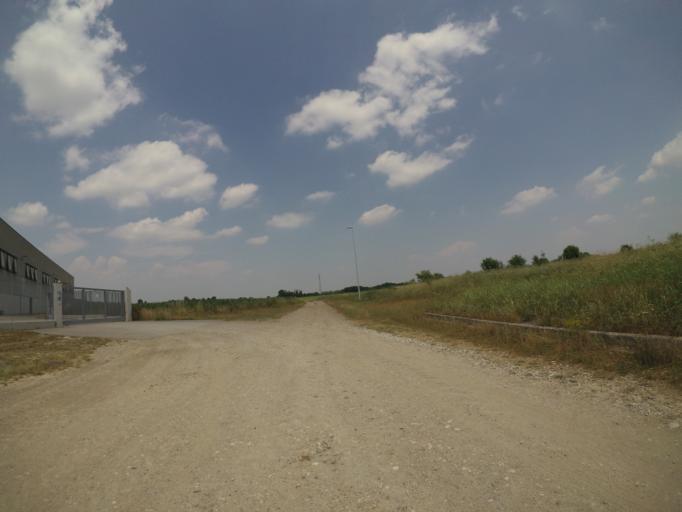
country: IT
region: Friuli Venezia Giulia
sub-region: Provincia di Udine
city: Bertiolo
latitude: 45.9513
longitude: 13.0600
